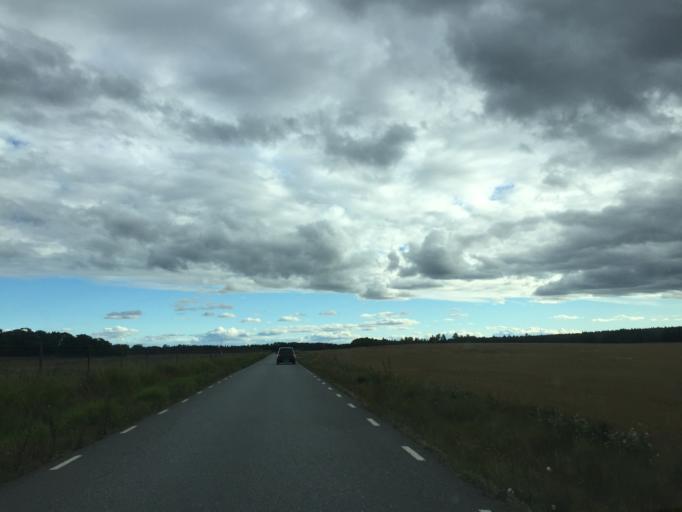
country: SE
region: OErebro
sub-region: Orebro Kommun
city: Hovsta
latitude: 59.3503
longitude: 15.1643
